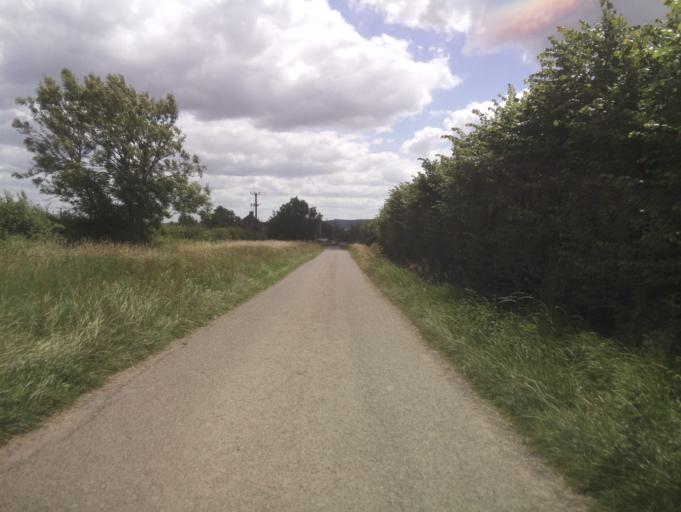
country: GB
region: England
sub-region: Oxfordshire
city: Faringdon
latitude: 51.6179
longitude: -1.6038
